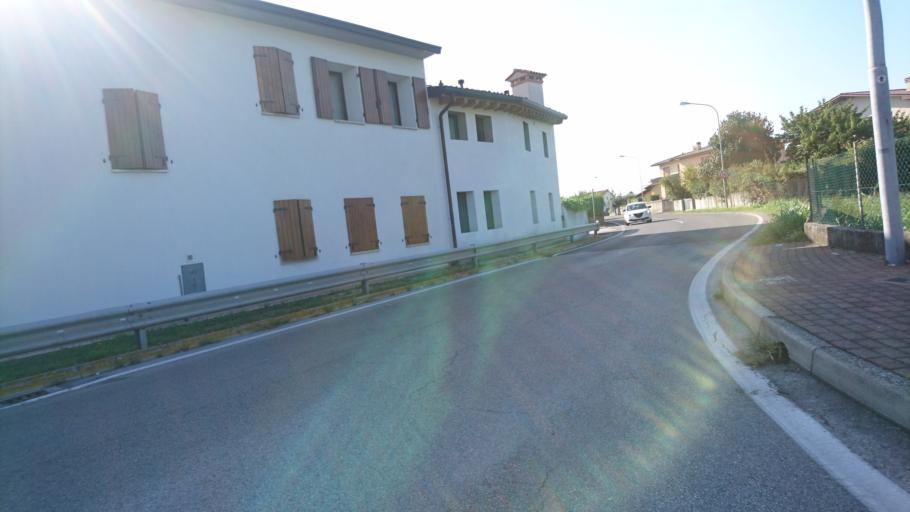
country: IT
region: Veneto
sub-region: Provincia di Vicenza
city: Bassano del Grappa
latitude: 45.7533
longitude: 11.7249
